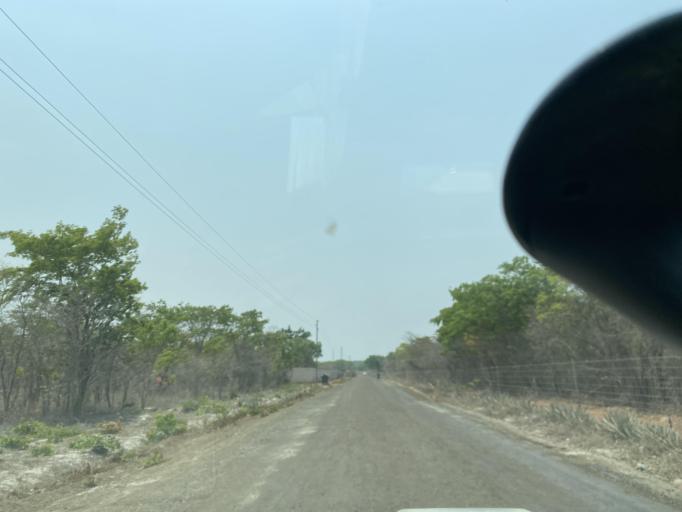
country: ZM
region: Lusaka
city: Lusaka
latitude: -15.5135
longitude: 28.4441
